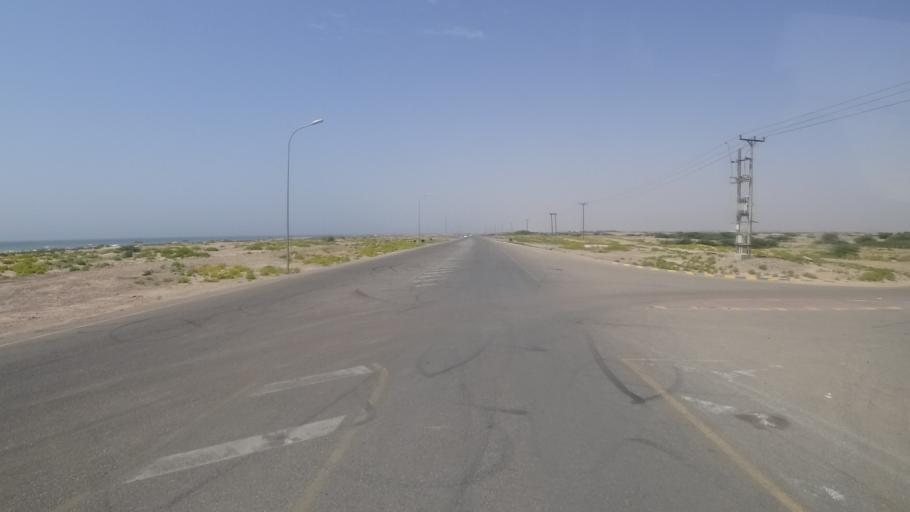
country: OM
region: Ash Sharqiyah
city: Sur
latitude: 22.1091
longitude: 59.7088
